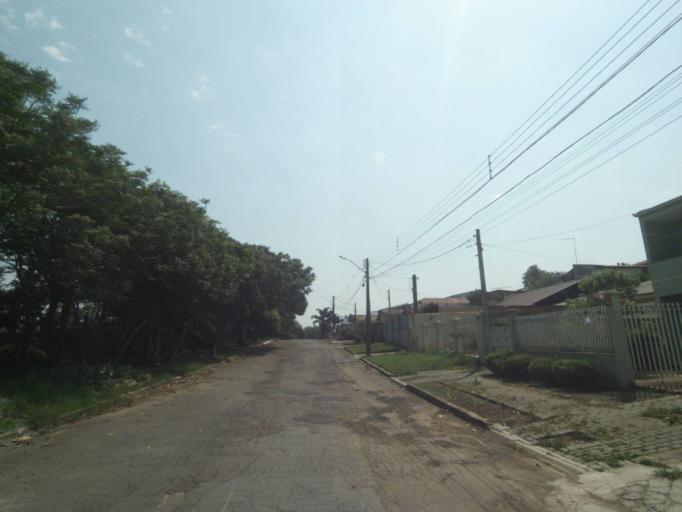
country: BR
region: Parana
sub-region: Sao Jose Dos Pinhais
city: Sao Jose dos Pinhais
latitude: -25.5447
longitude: -49.2472
